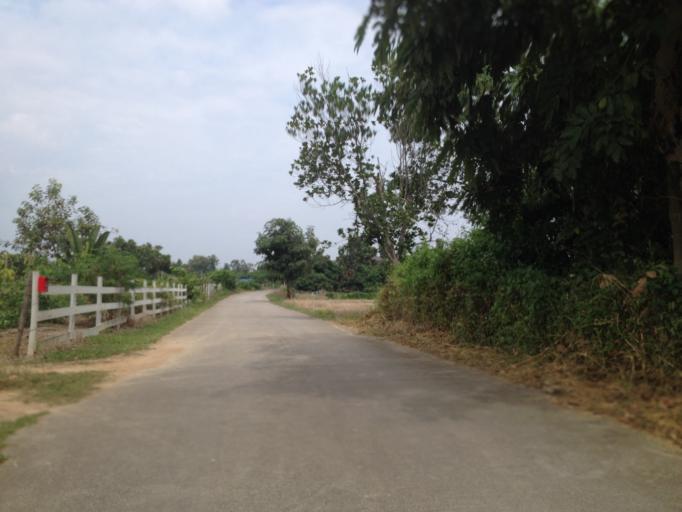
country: TH
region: Chiang Mai
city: San Pa Tong
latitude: 18.6611
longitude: 98.8741
